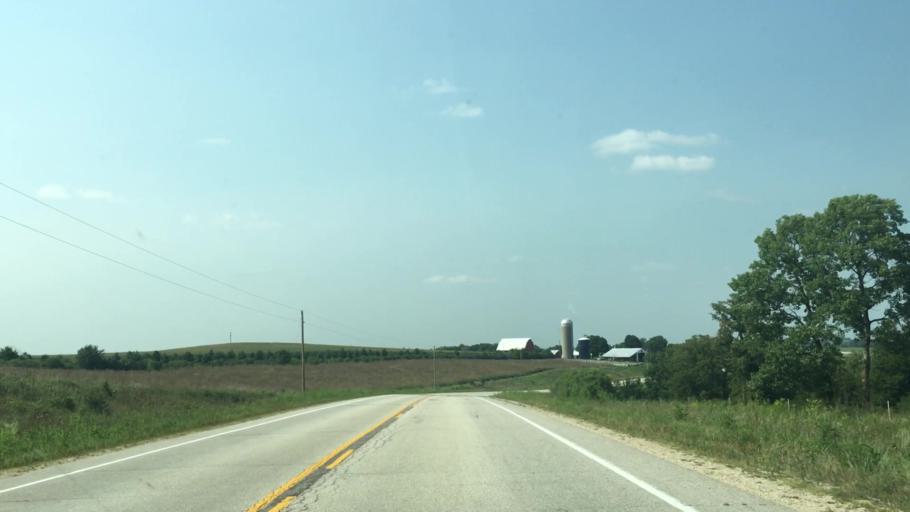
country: US
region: Minnesota
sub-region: Fillmore County
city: Harmony
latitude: 43.6789
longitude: -91.9408
